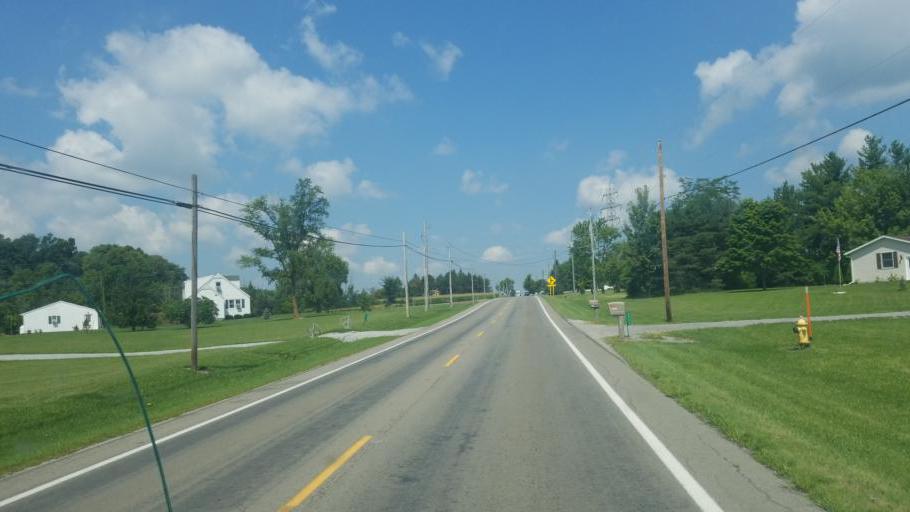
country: US
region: Ohio
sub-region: Allen County
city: Lima
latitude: 40.6999
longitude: -83.9906
